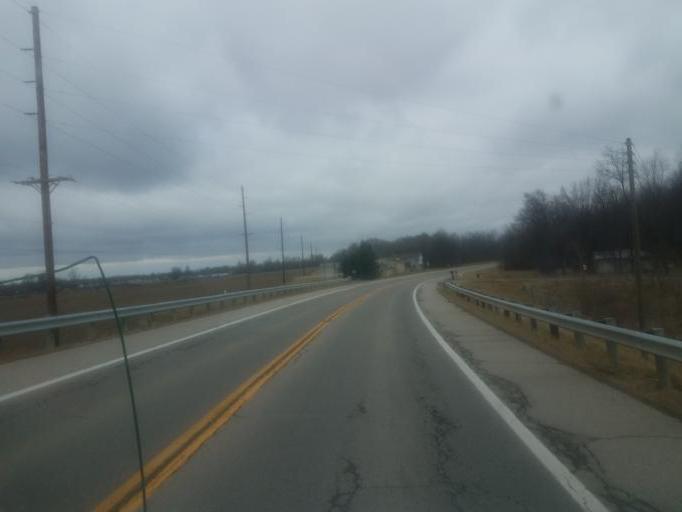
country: US
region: Ohio
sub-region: Crawford County
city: Crestline
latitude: 40.7642
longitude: -82.7461
